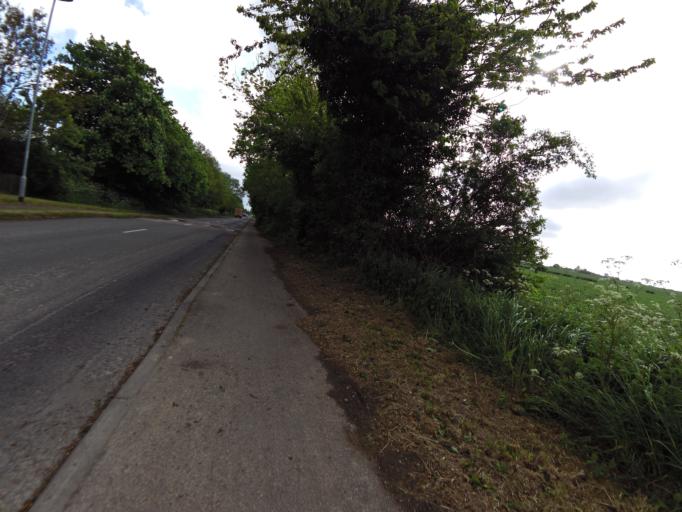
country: GB
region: England
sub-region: Cambridgeshire
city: Bottisham
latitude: 52.2203
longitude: 0.2538
